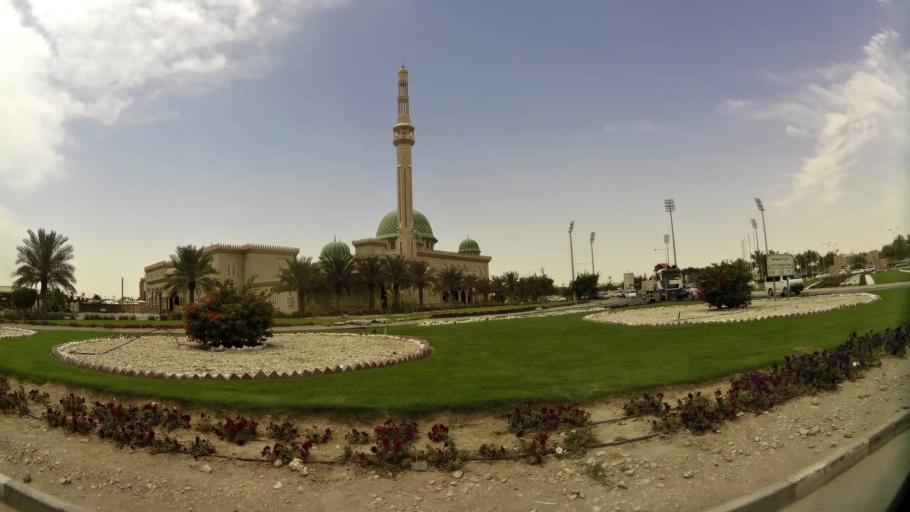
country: QA
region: Baladiyat ar Rayyan
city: Ar Rayyan
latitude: 25.2830
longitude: 51.4331
